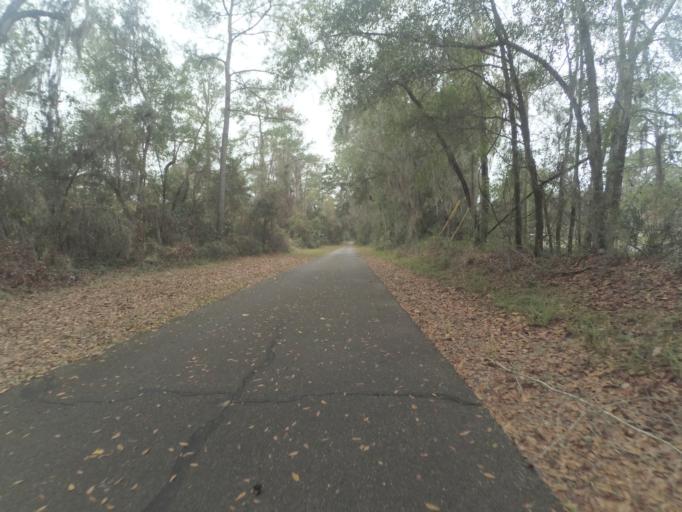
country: US
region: Florida
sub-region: Alachua County
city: Gainesville
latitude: 29.5955
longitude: -82.2176
